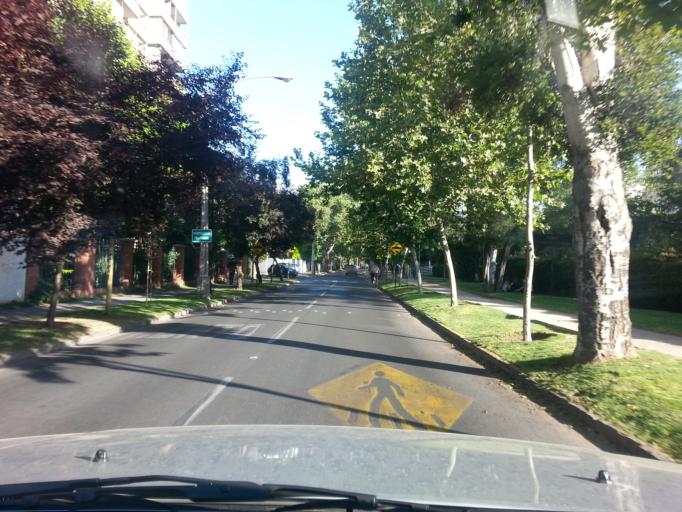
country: CL
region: Santiago Metropolitan
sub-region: Provincia de Santiago
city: Villa Presidente Frei, Nunoa, Santiago, Chile
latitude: -33.4273
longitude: -70.5891
